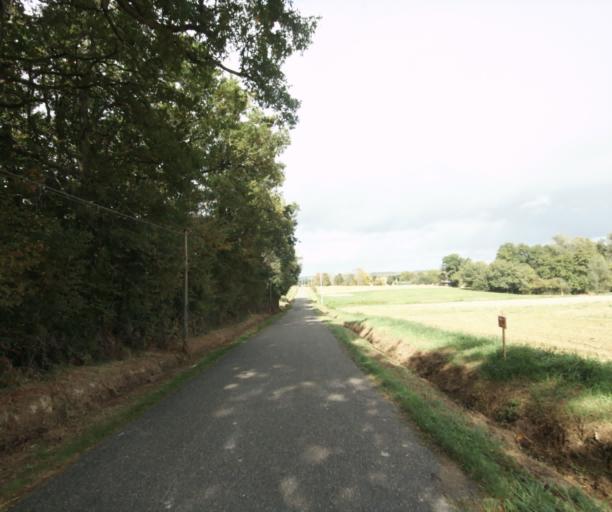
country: FR
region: Midi-Pyrenees
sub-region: Departement du Gers
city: Cazaubon
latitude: 43.8564
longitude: -0.0192
